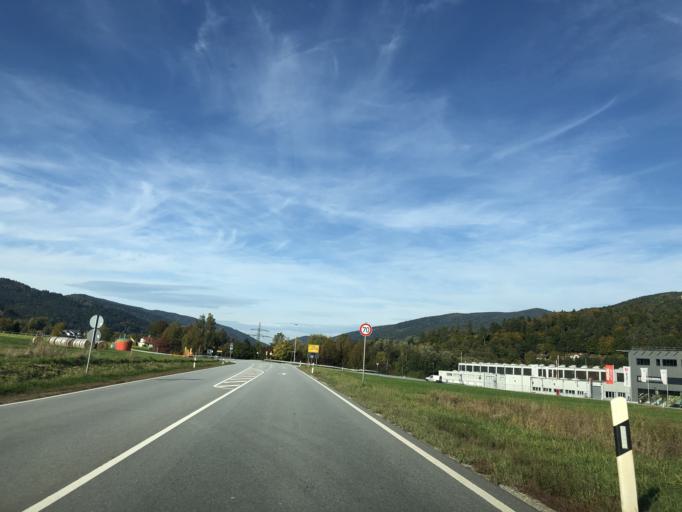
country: DE
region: Bavaria
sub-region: Lower Bavaria
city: Deggendorf
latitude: 48.8572
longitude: 12.9597
